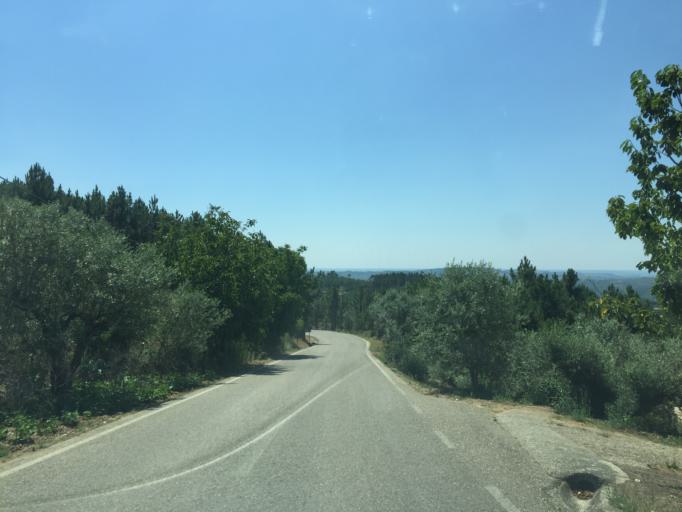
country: PT
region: Santarem
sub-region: Ferreira do Zezere
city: Ferreira do Zezere
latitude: 39.5979
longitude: -8.3012
